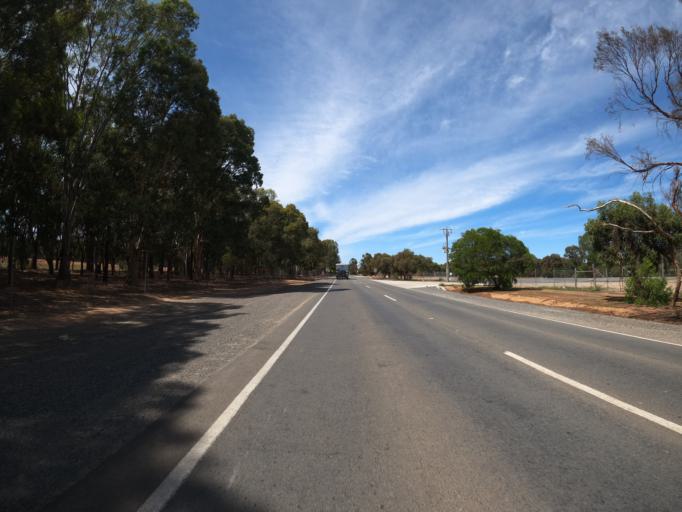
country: AU
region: Victoria
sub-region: Moira
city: Yarrawonga
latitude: -36.0343
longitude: 145.9955
